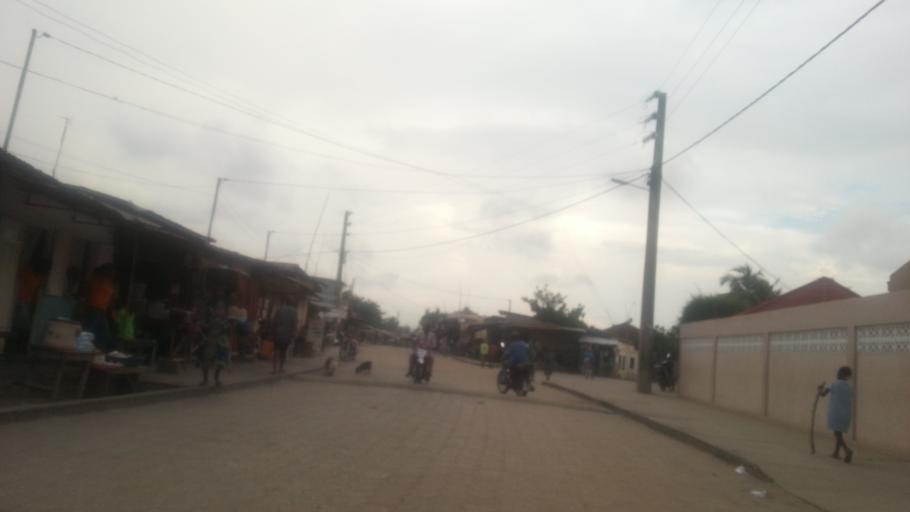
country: BJ
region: Queme
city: Porto-Novo
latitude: 6.3930
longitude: 2.5407
